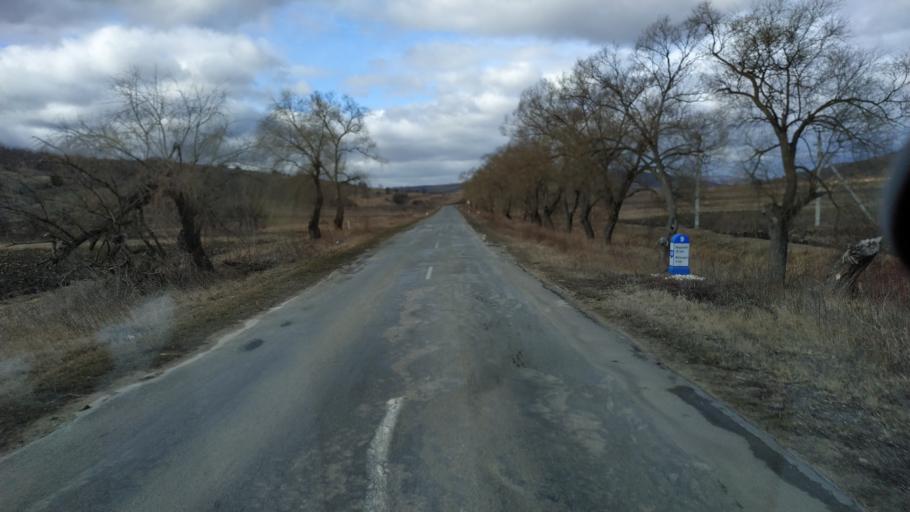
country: MD
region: Stinga Nistrului
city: Bucovat
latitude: 47.1426
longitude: 28.3713
